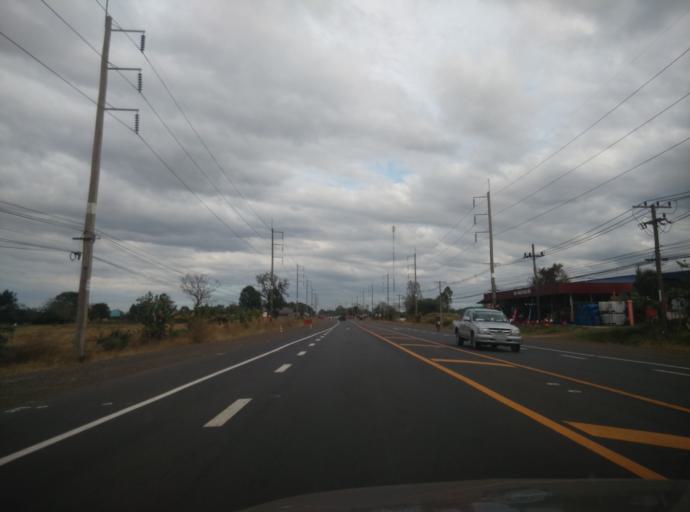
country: TH
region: Sisaket
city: Uthumphon Phisai
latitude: 15.1531
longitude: 104.2006
